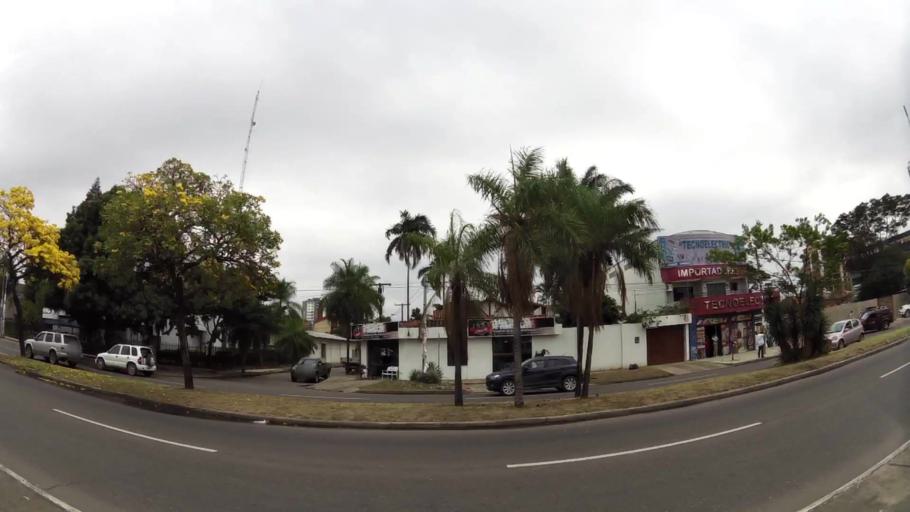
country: BO
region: Santa Cruz
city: Santa Cruz de la Sierra
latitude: -17.7773
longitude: -63.1652
